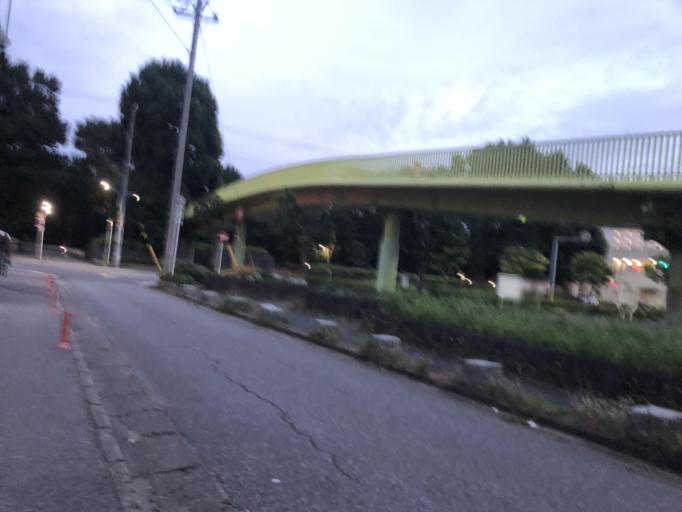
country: JP
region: Chiba
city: Funabashi
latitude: 35.7203
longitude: 139.9710
